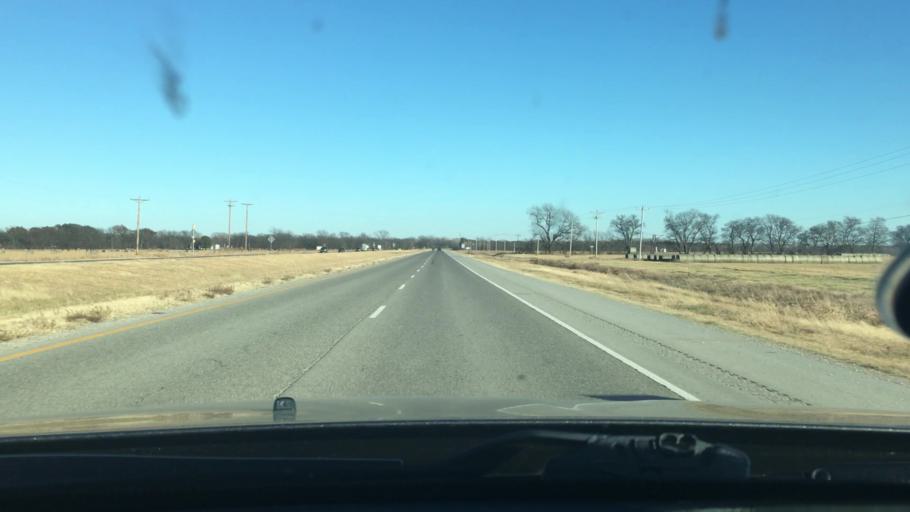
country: US
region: Oklahoma
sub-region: Murray County
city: Davis
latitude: 34.5064
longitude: -97.1686
